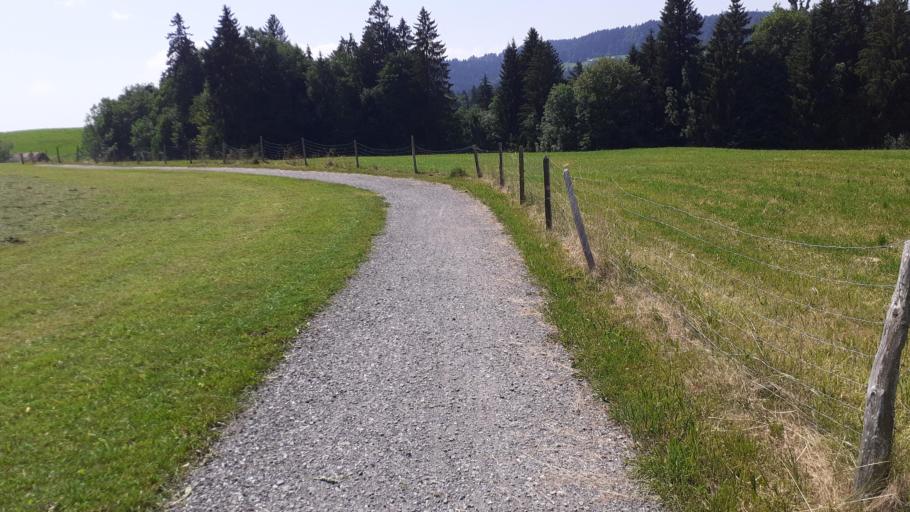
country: AT
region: Vorarlberg
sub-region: Politischer Bezirk Bregenz
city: Doren
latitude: 47.4585
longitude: 9.8477
